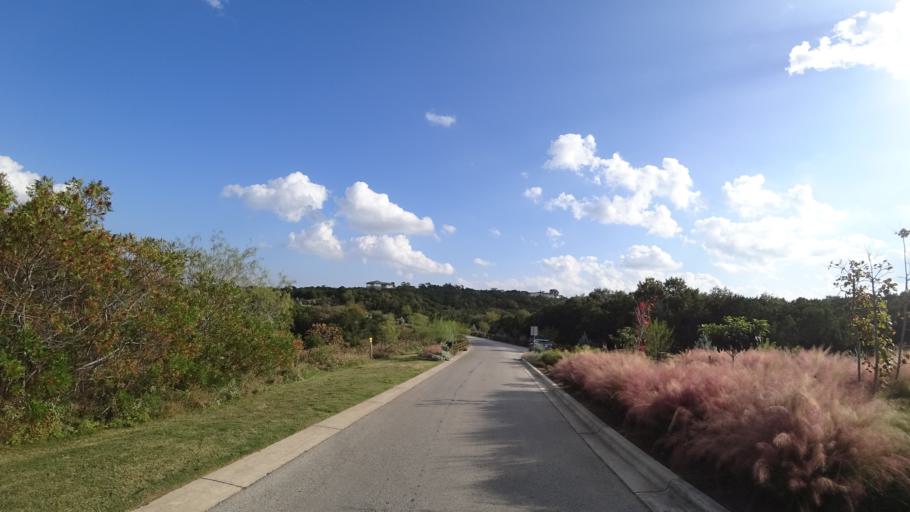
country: US
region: Texas
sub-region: Travis County
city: Barton Creek
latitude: 30.2744
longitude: -97.8839
